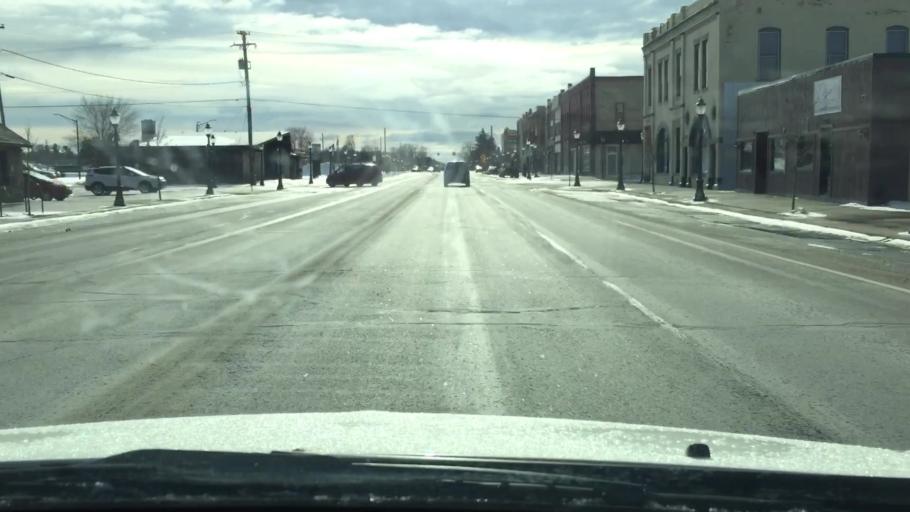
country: US
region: Michigan
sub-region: Kalkaska County
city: Kalkaska
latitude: 44.7327
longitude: -85.1769
